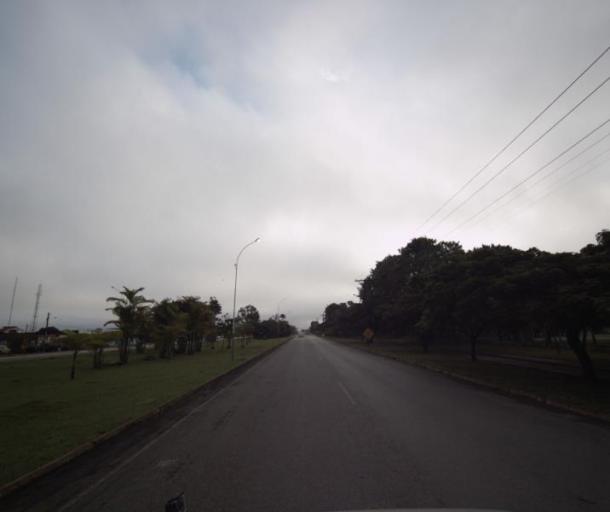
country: BR
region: Goias
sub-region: Pirenopolis
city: Pirenopolis
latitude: -15.7897
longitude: -48.7720
